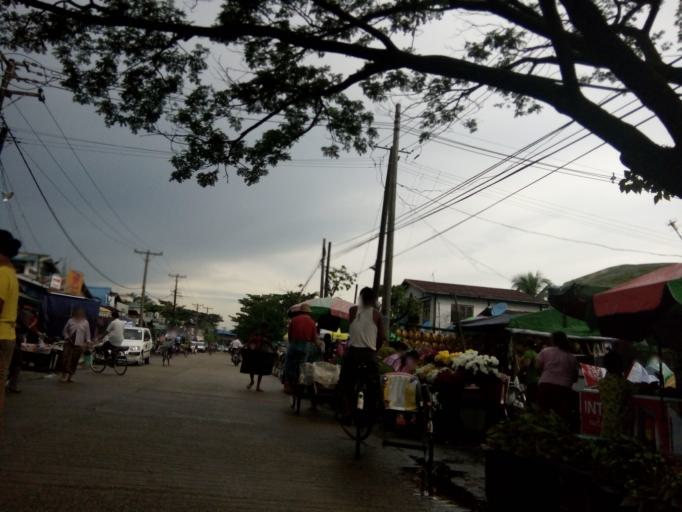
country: MM
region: Yangon
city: Yangon
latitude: 16.9245
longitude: 96.1589
